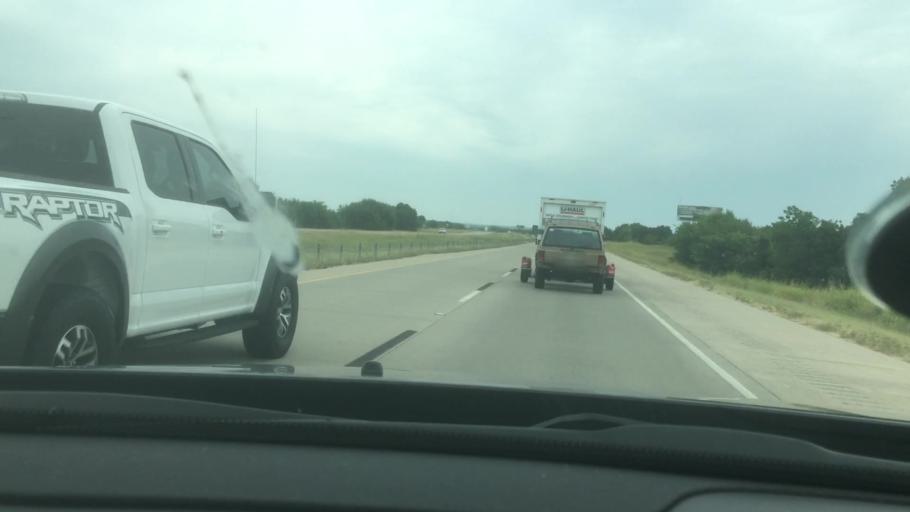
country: US
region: Oklahoma
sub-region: Carter County
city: Ardmore
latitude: 34.2775
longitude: -97.1609
